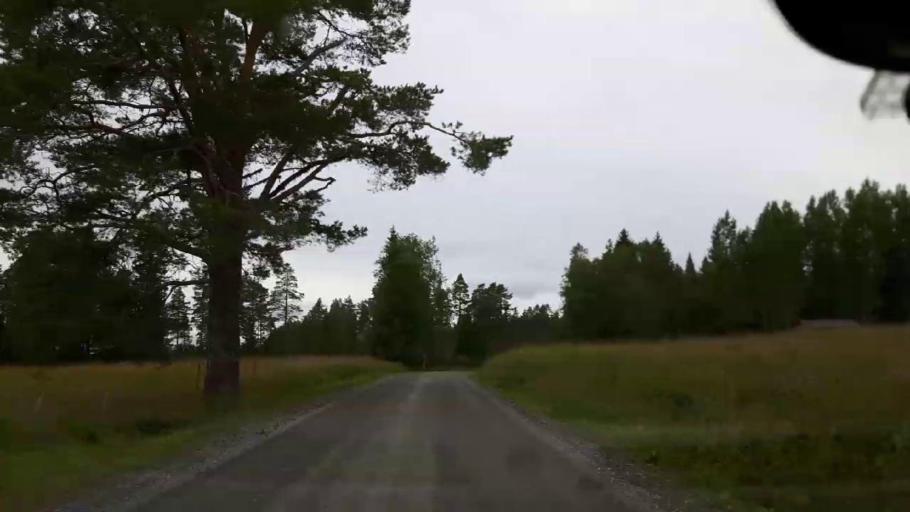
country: SE
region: Jaemtland
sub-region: Krokoms Kommun
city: Krokom
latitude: 63.2915
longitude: 14.3765
